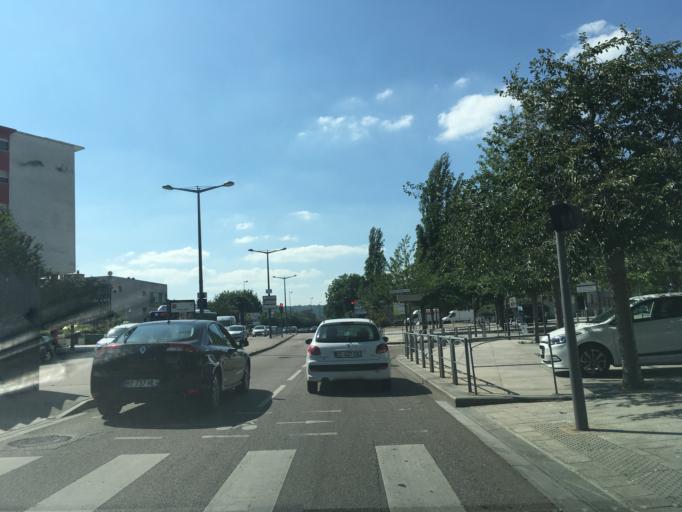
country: FR
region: Lorraine
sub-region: Departement de Meurthe-et-Moselle
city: Villers-les-Nancy
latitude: 48.6668
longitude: 6.1659
